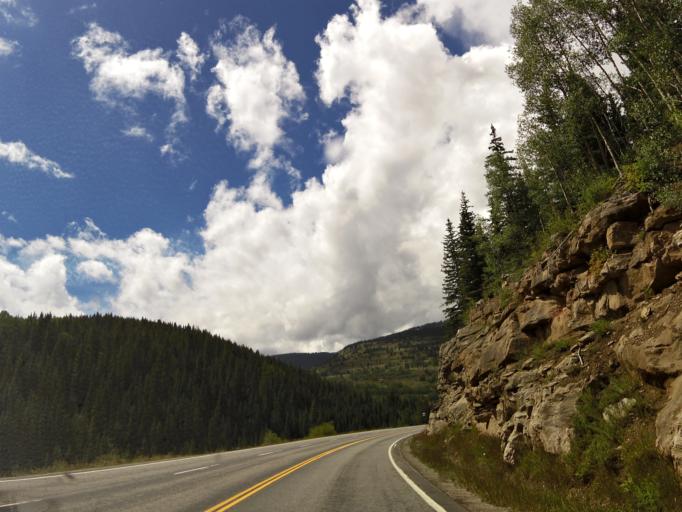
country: US
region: Colorado
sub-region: San Juan County
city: Silverton
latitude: 37.7264
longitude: -107.7354
